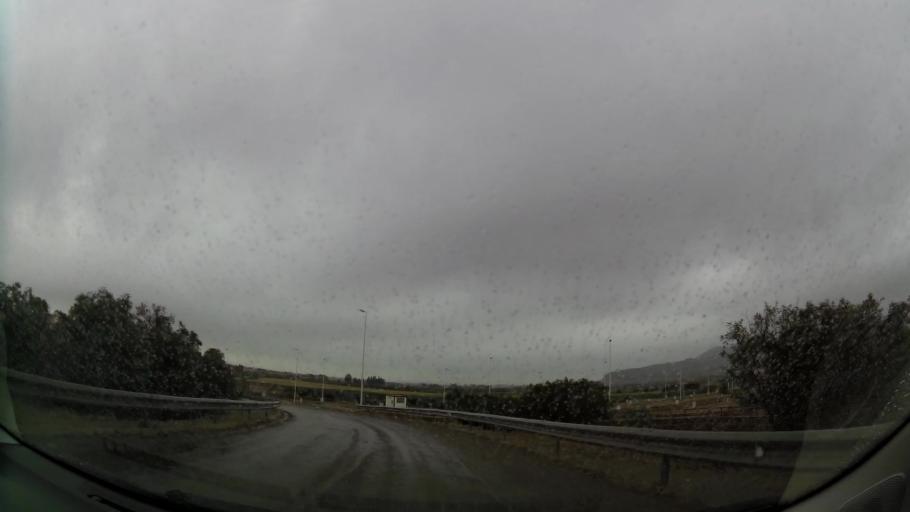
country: MA
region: Oriental
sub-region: Nador
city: Nador
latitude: 35.1535
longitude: -2.9755
